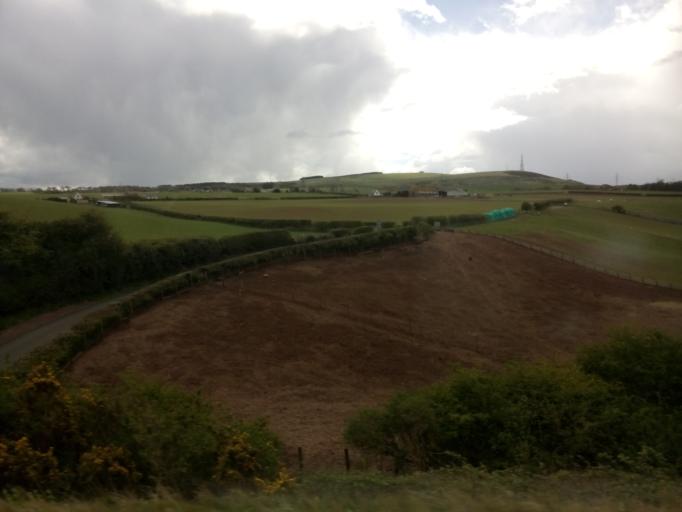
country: GB
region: Scotland
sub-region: East Lothian
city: Dunbar
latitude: 55.9599
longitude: -2.4117
